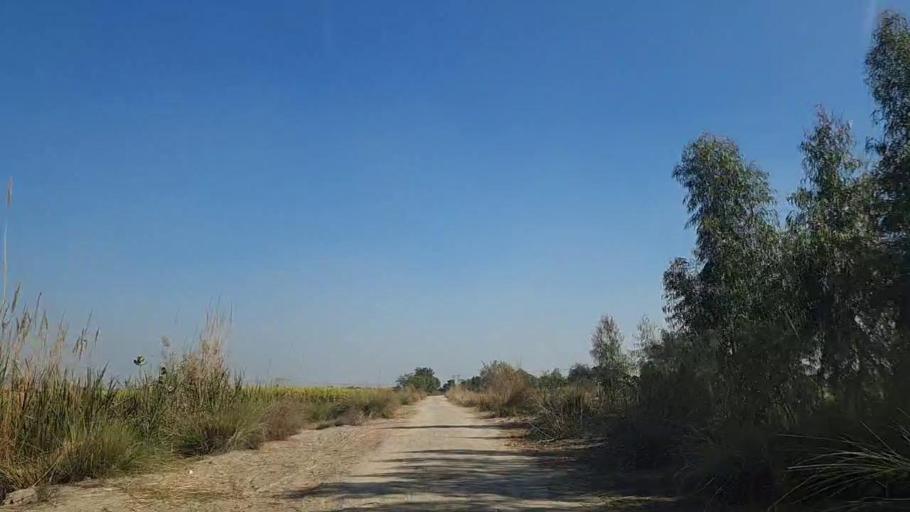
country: PK
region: Sindh
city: Sakrand
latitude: 26.2458
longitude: 68.1983
